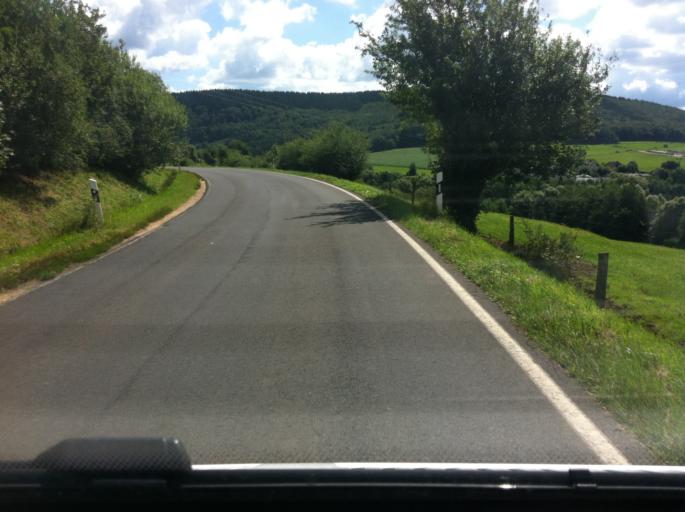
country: DE
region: Rheinland-Pfalz
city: Kalenborn-Scheuern
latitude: 50.2471
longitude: 6.5862
